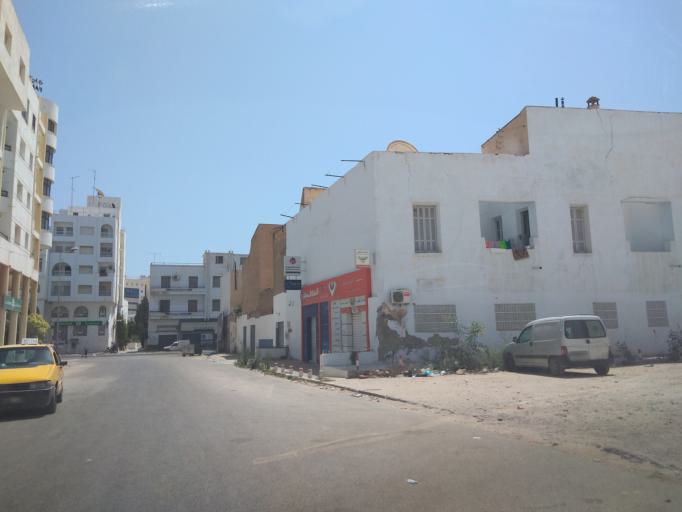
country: TN
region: Safaqis
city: Sfax
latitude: 34.7362
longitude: 10.7532
